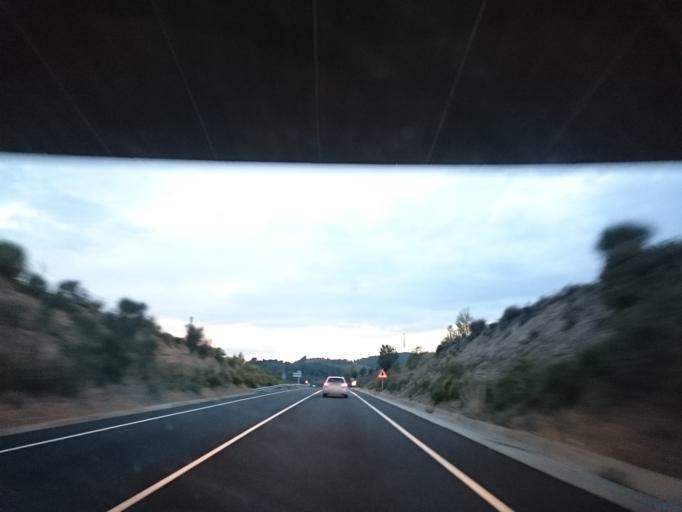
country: ES
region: Catalonia
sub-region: Provincia de Barcelona
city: Sant Pere de Riudebitlles
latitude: 41.4505
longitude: 1.6844
